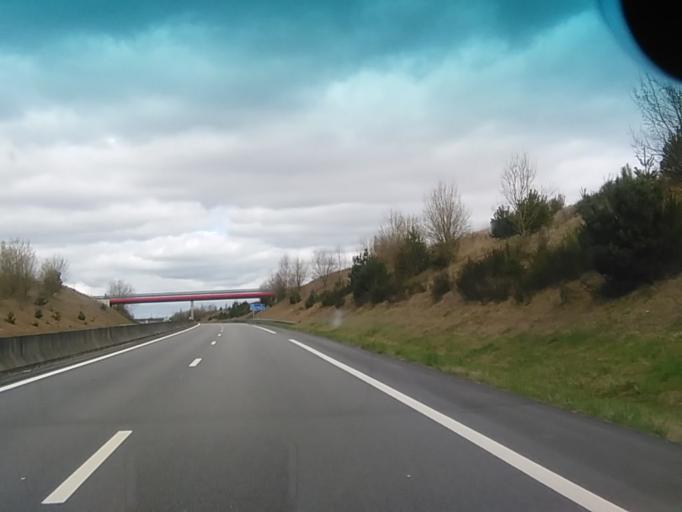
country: FR
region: Haute-Normandie
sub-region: Departement de l'Eure
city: Bourg-Achard
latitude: 49.3430
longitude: 0.8349
